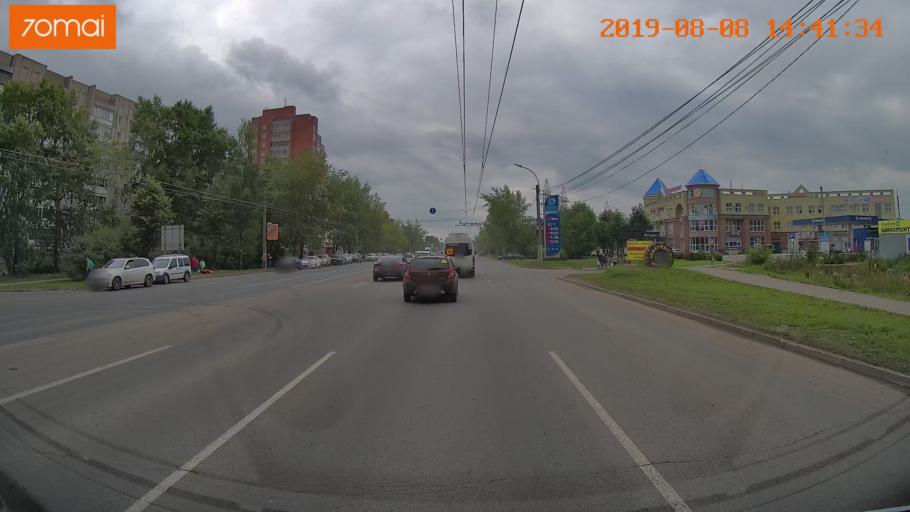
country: RU
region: Ivanovo
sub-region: Gorod Ivanovo
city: Ivanovo
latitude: 56.9565
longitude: 40.9743
